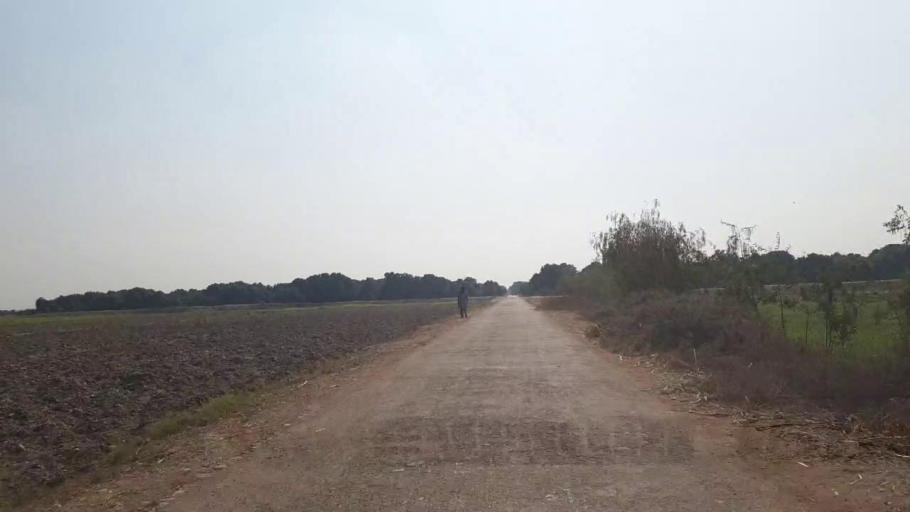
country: PK
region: Sindh
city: Chambar
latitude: 25.3913
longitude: 68.8958
